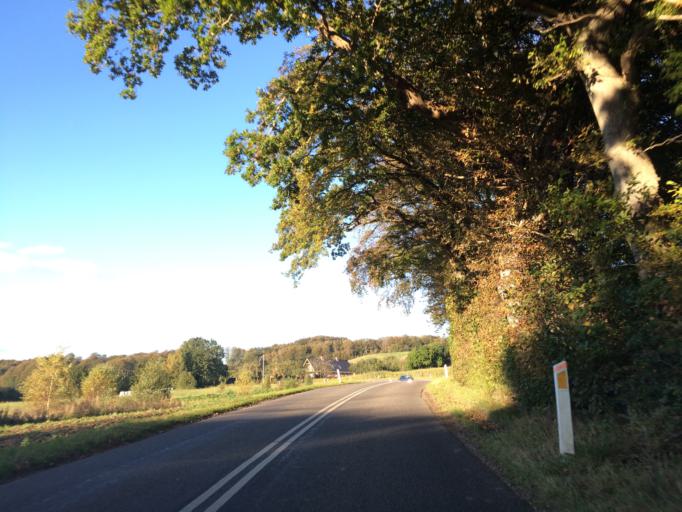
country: DK
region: Central Jutland
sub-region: Skanderborg Kommune
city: Ry
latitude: 56.1196
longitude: 9.7341
